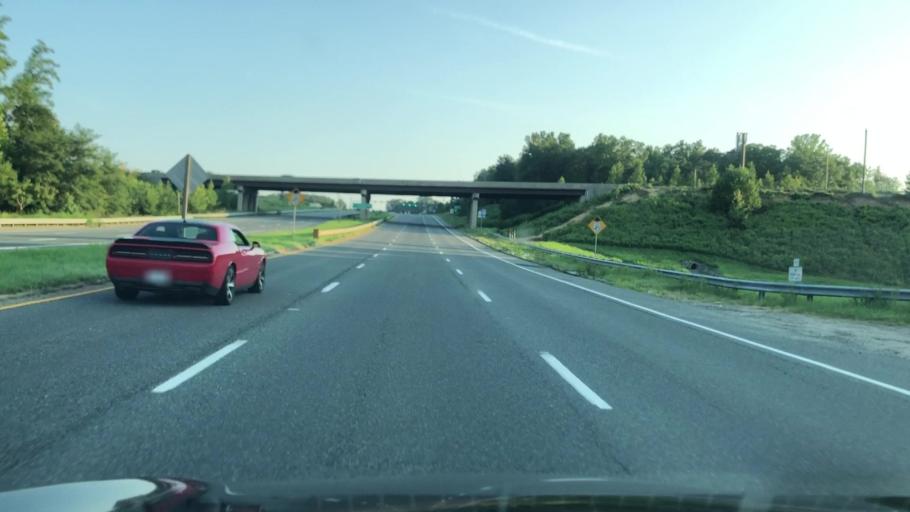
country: US
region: Virginia
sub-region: Stafford County
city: Falmouth
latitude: 38.3712
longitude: -77.4542
